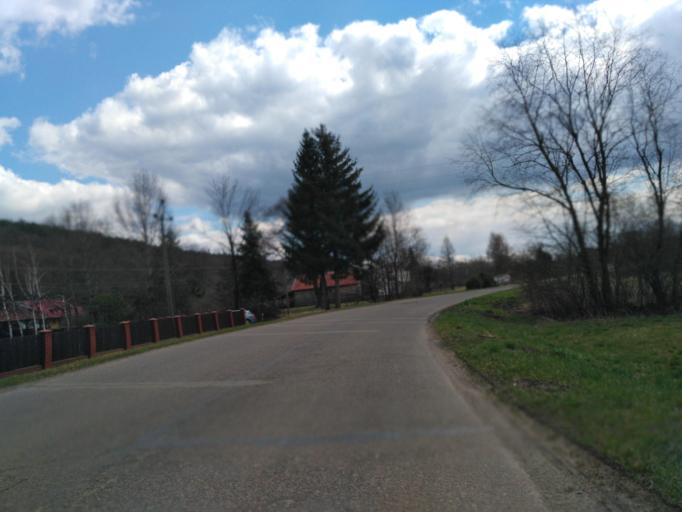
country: PL
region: Subcarpathian Voivodeship
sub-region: Powiat sanocki
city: Tyrawa Woloska
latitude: 49.6023
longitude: 22.3126
